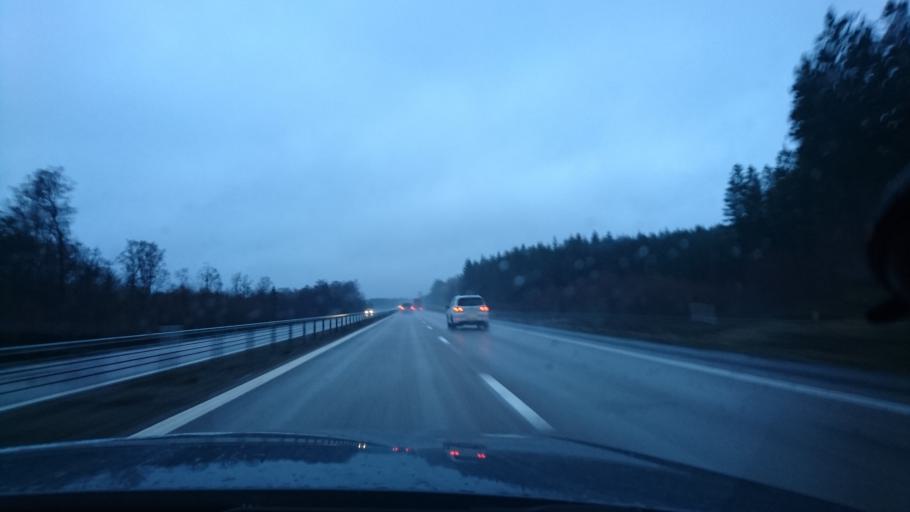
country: SE
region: Skane
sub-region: Orkelljunga Kommun
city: OErkelljunga
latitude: 56.3113
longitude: 13.4072
